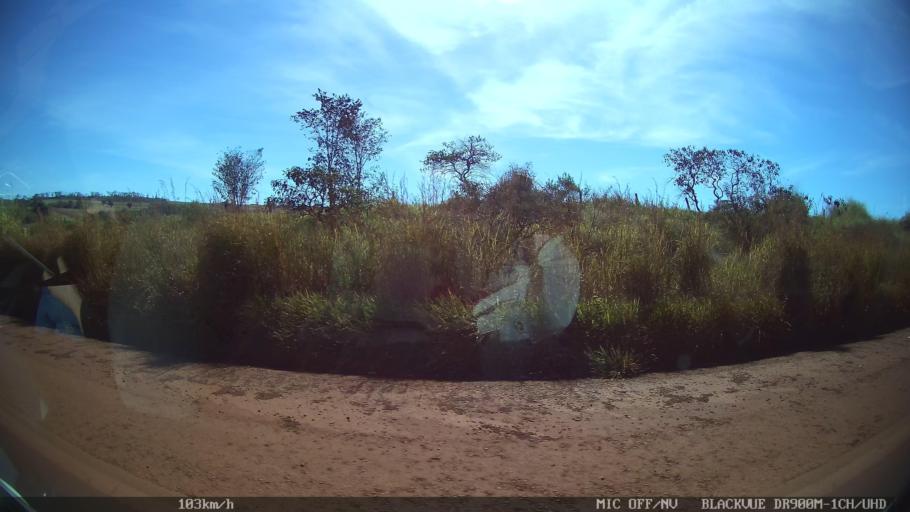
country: BR
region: Sao Paulo
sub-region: Sao Joaquim Da Barra
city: Sao Joaquim da Barra
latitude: -20.5518
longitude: -47.6588
